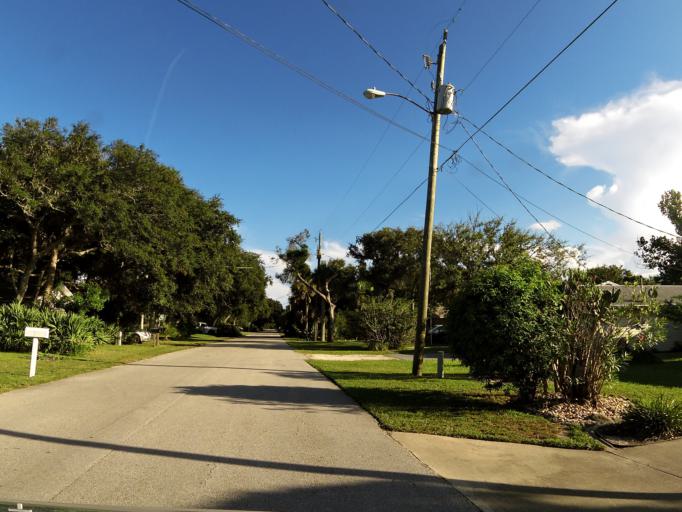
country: US
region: Florida
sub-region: Flagler County
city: Flagler Beach
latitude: 29.4600
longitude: -81.1210
